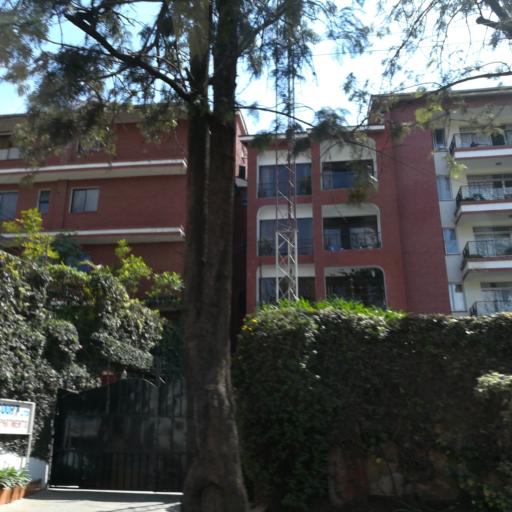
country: KE
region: Nairobi Area
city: Nairobi
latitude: -1.2941
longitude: 36.7961
